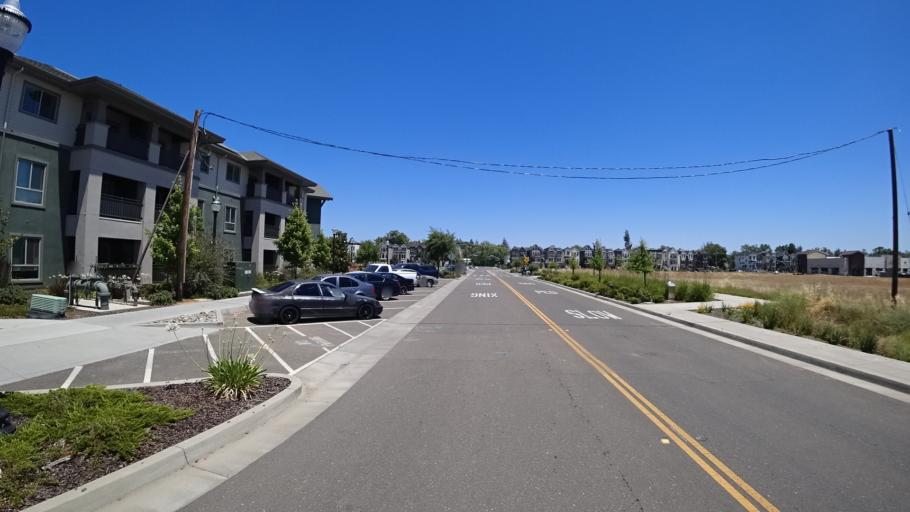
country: US
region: California
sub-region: Sacramento County
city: Sacramento
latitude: 38.5425
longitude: -121.4845
